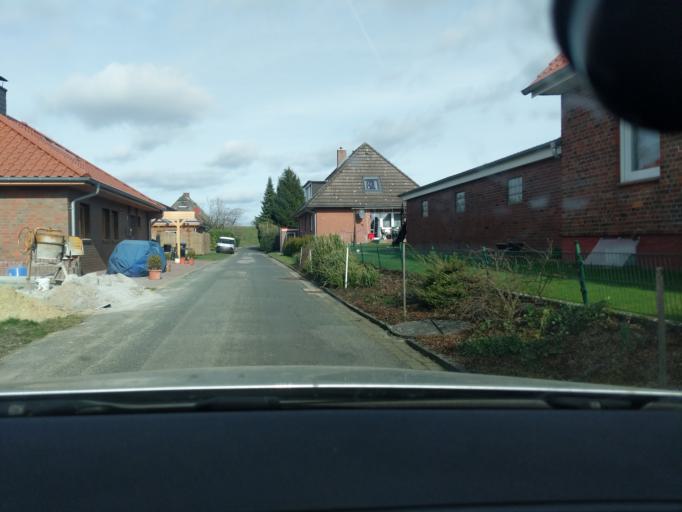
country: DE
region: Lower Saxony
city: Drochtersen
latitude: 53.7123
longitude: 9.3911
